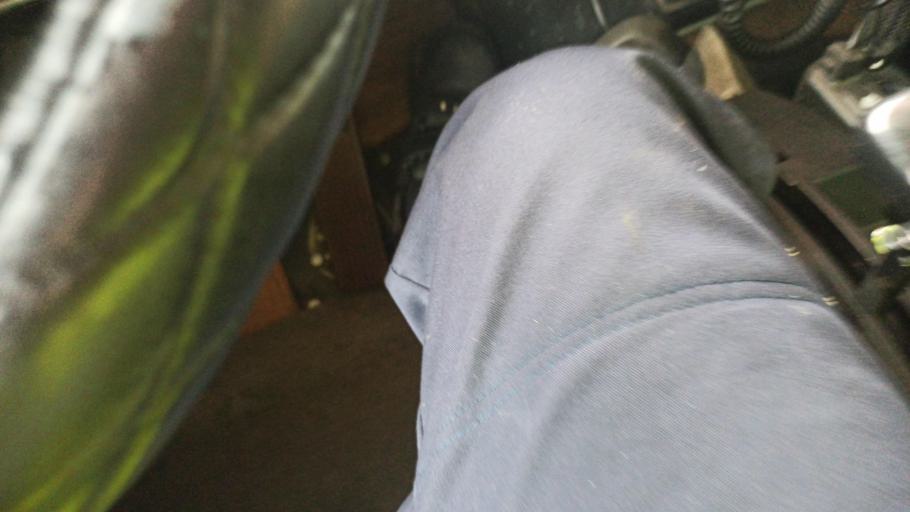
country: RU
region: Republic of Karelia
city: Kostomuksha
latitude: 64.8025
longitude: 30.7143
